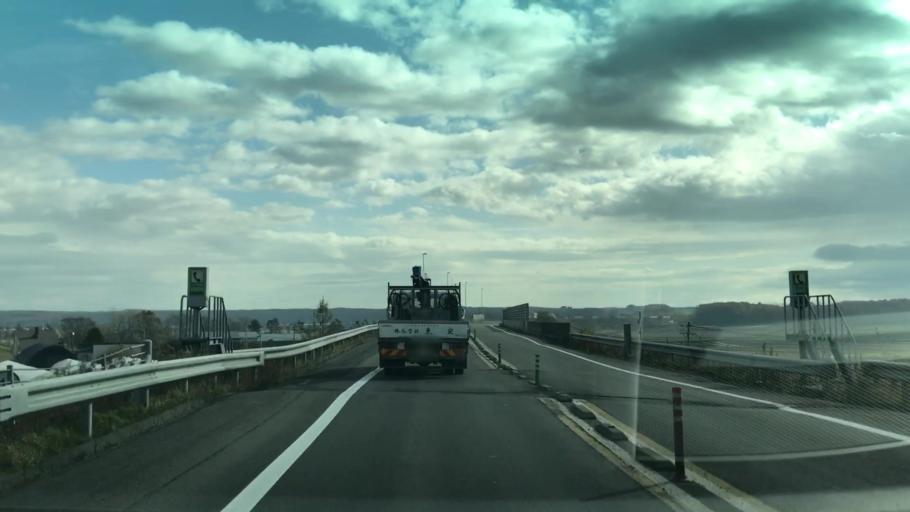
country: JP
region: Hokkaido
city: Tomakomai
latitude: 42.5759
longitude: 141.9675
